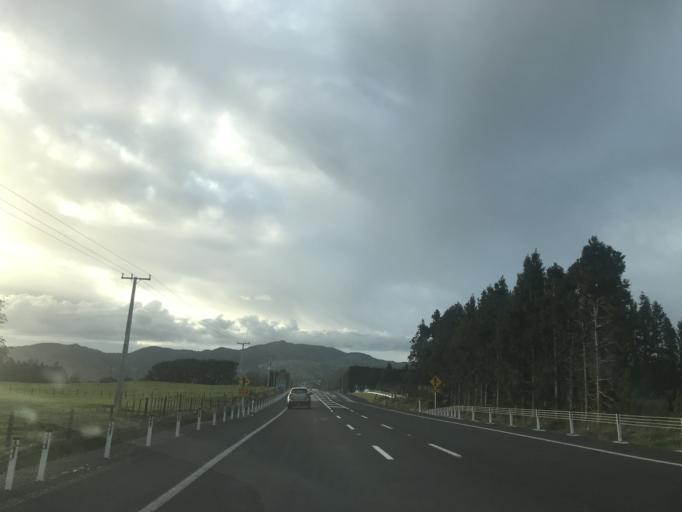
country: NZ
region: Waikato
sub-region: Hauraki District
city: Waihi
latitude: -37.4113
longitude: 175.8629
